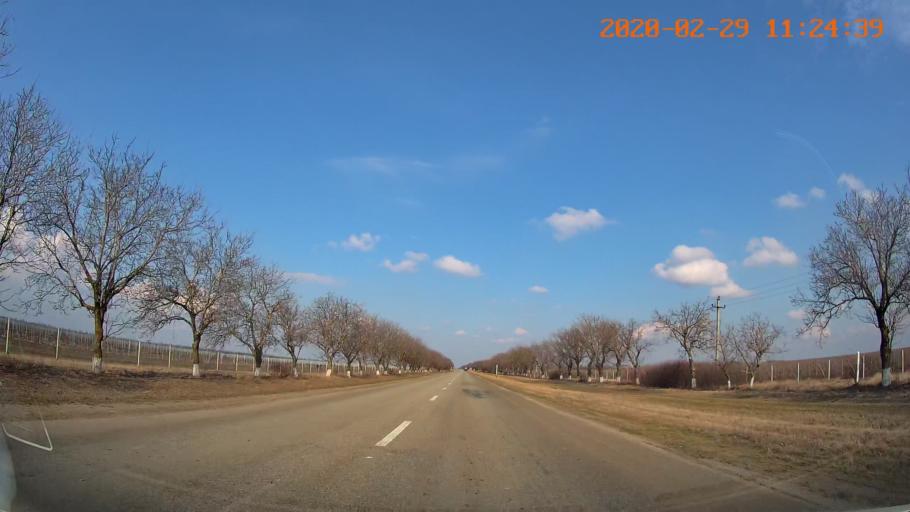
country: MD
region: Telenesti
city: Cocieri
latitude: 47.4271
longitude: 29.1537
